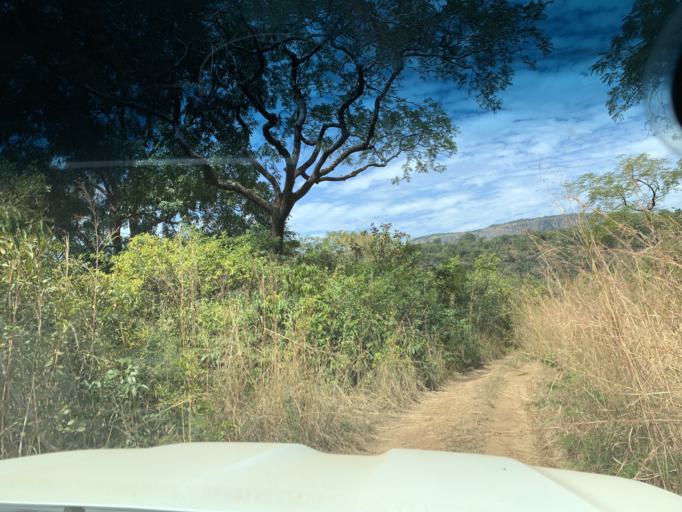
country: GN
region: Mamou
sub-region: Pita
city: Pita
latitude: 10.9962
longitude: -12.4901
